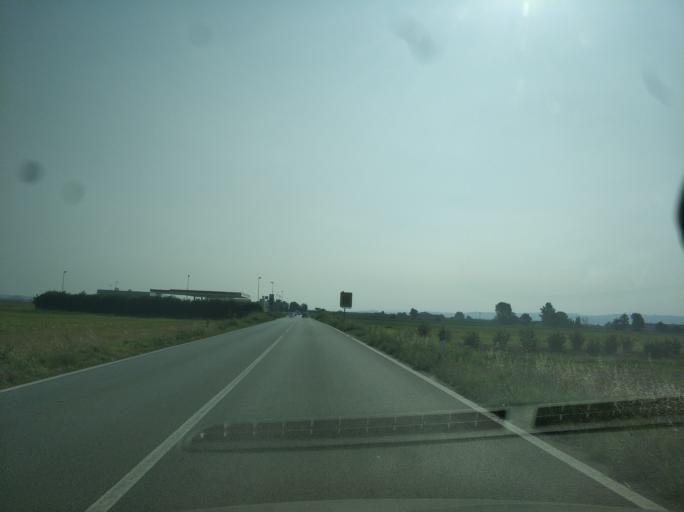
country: IT
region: Piedmont
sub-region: Provincia di Cuneo
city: Roreto
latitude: 44.6675
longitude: 7.8154
